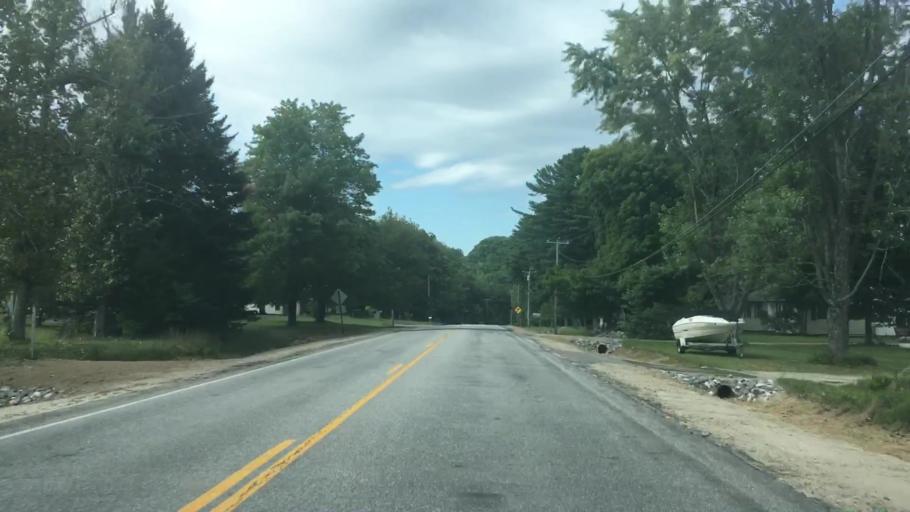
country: US
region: Maine
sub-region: Cumberland County
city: Raymond
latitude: 43.9866
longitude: -70.5196
